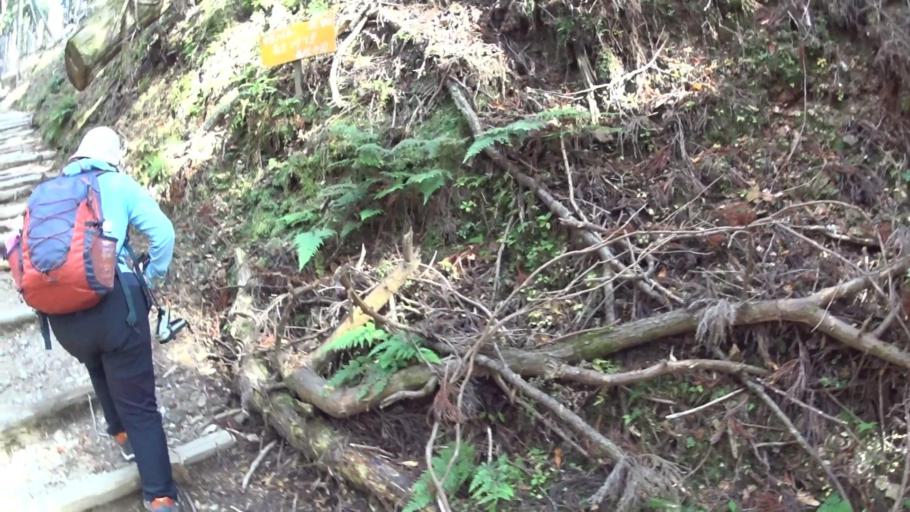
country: JP
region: Kyoto
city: Kameoka
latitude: 35.0547
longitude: 135.6333
